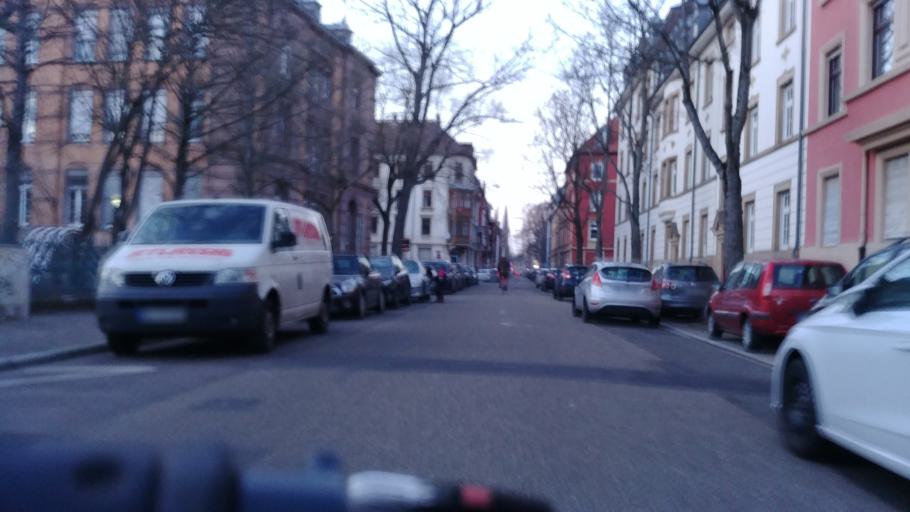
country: DE
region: Baden-Wuerttemberg
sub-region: Karlsruhe Region
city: Karlsruhe
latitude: 48.9966
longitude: 8.4085
